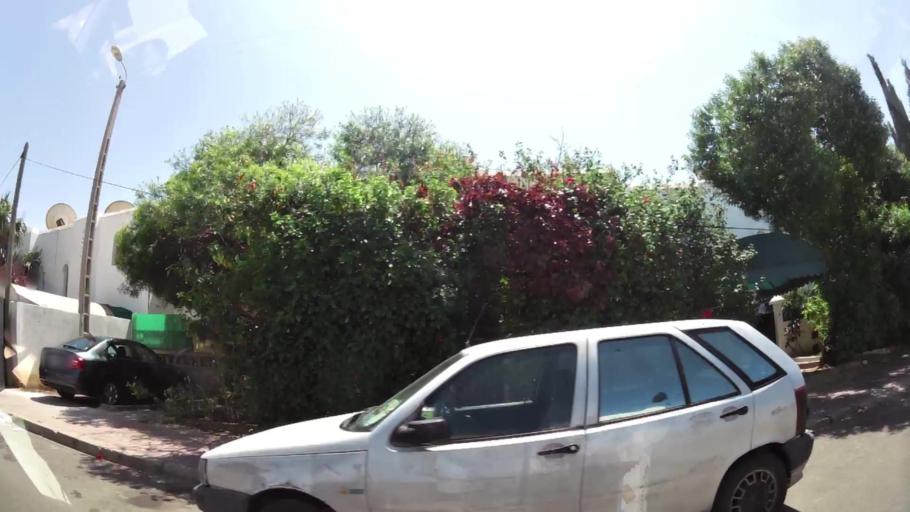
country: MA
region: Souss-Massa-Draa
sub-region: Agadir-Ida-ou-Tnan
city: Agadir
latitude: 30.4341
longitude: -9.5906
